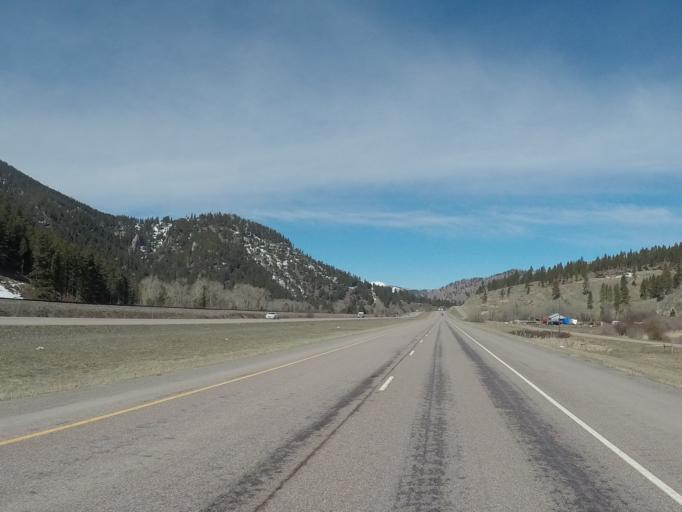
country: US
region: Montana
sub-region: Missoula County
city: Clinton
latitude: 46.6993
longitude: -113.4919
